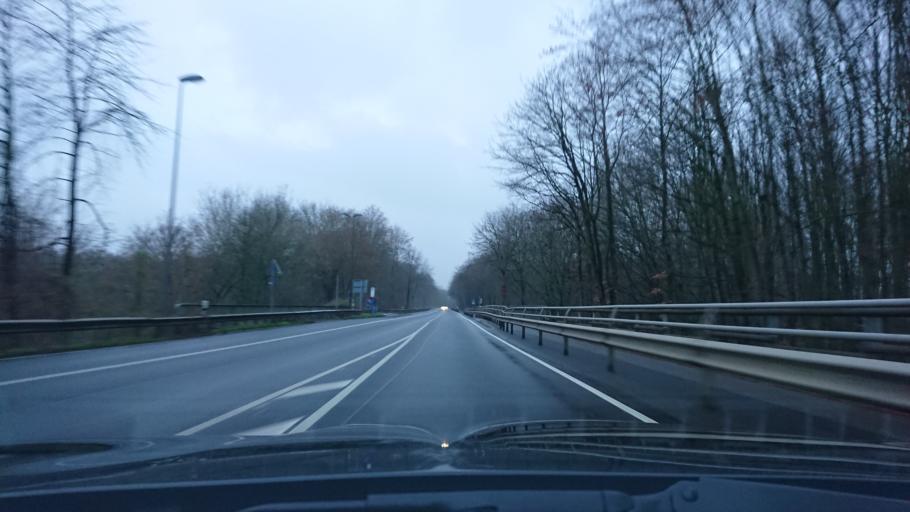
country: DE
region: North Rhine-Westphalia
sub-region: Regierungsbezirk Koln
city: Bonn
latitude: 50.7705
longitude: 7.0945
